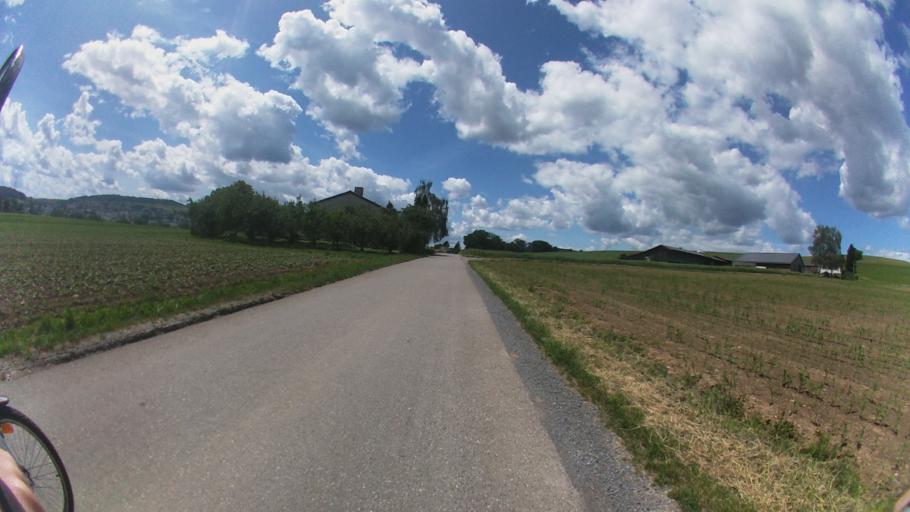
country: CH
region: Zurich
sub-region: Bezirk Dielsdorf
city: Dielsdorf
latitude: 47.4938
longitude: 8.4700
